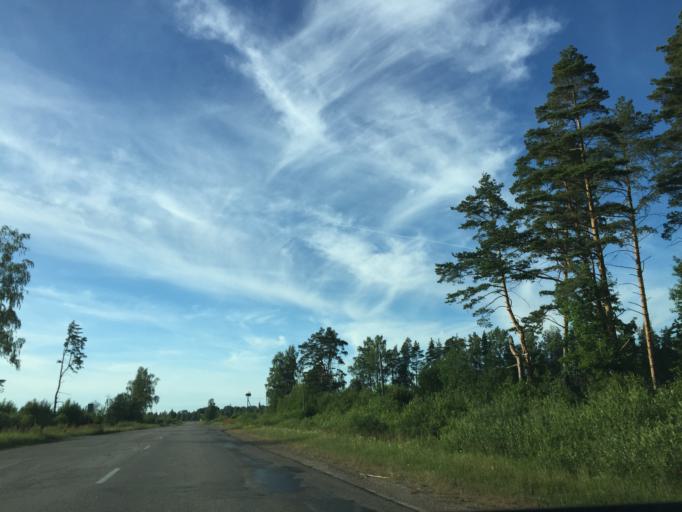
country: LV
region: Ventspils
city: Ventspils
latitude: 57.2949
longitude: 21.5633
